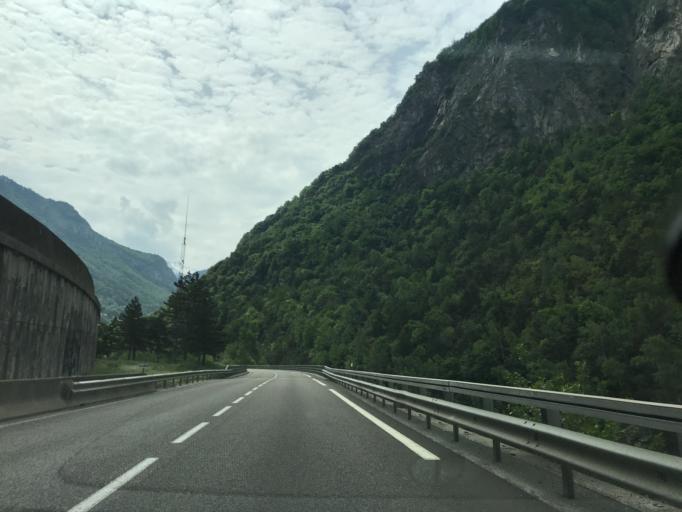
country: FR
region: Rhone-Alpes
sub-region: Departement de la Savoie
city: Moutiers
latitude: 45.4887
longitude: 6.5195
